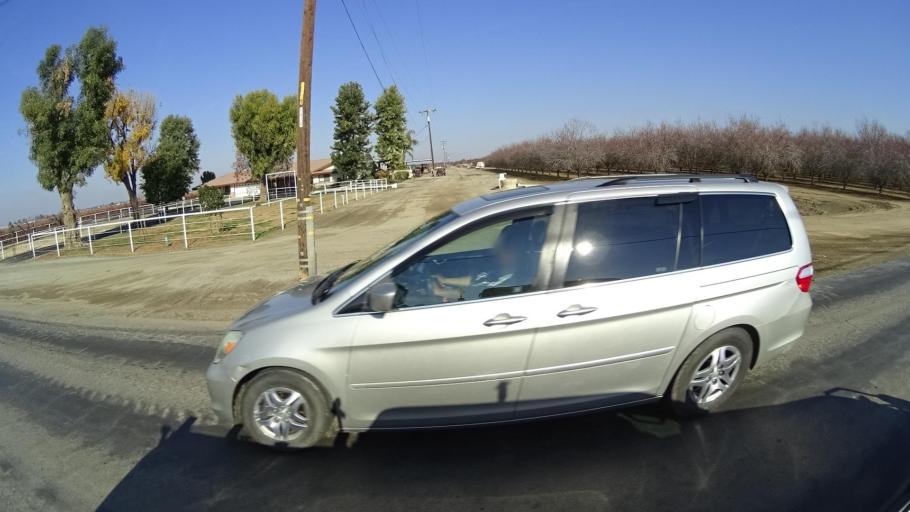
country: US
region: California
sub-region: Kern County
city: Weedpatch
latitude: 35.2379
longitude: -118.9008
